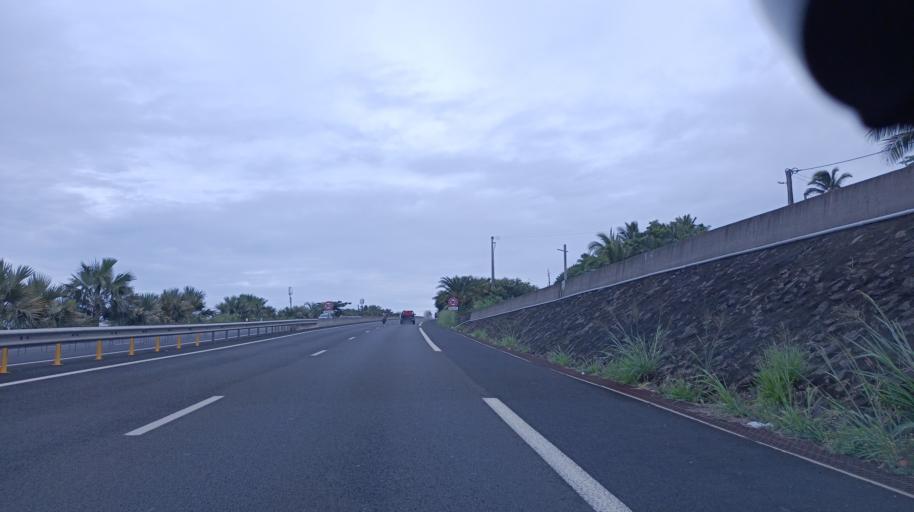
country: RE
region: Reunion
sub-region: Reunion
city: Petite-Ile
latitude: -21.3579
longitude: 55.5316
